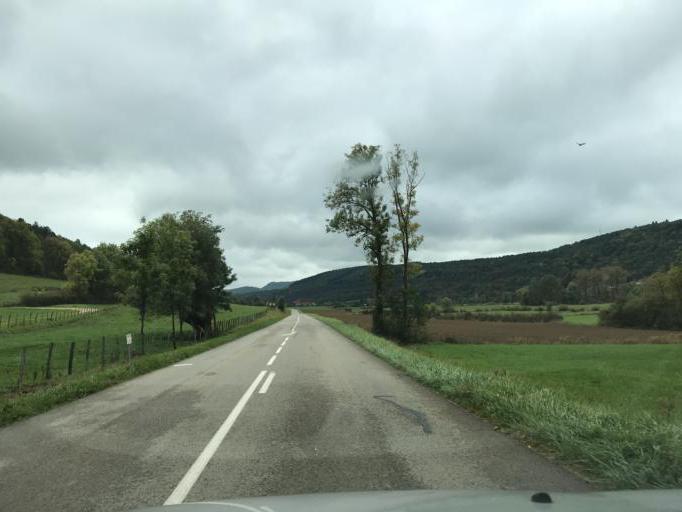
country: FR
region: Rhone-Alpes
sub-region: Departement de l'Ain
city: Coligny
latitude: 46.3843
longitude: 5.4460
